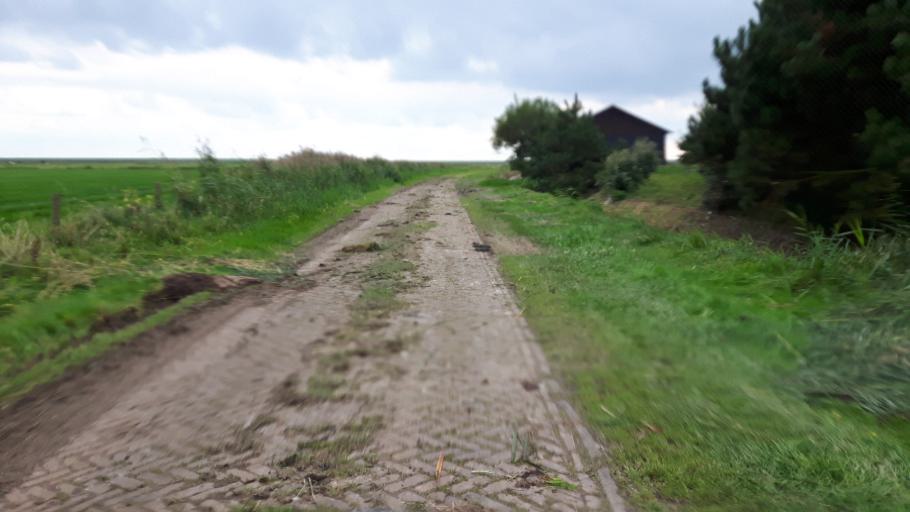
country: NL
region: Friesland
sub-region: Gemeente Ameland
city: Nes
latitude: 53.4490
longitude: 5.8190
